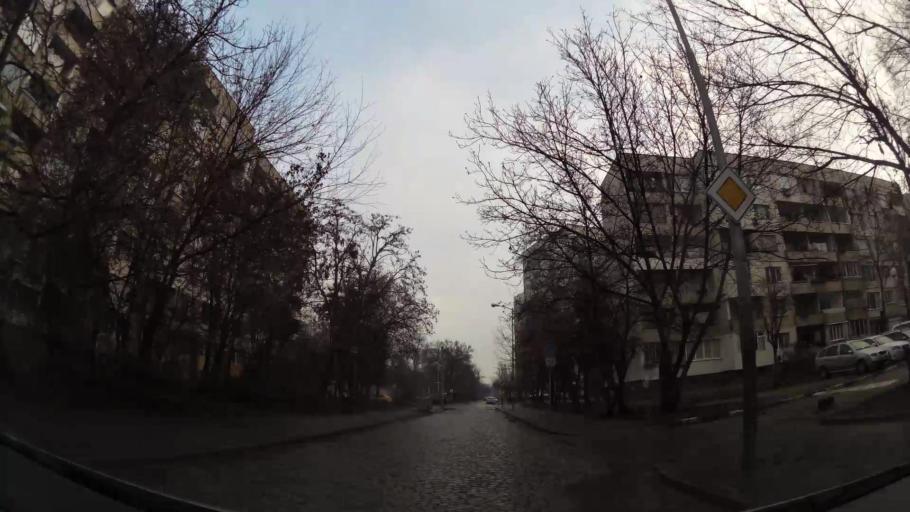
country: BG
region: Sofia-Capital
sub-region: Stolichna Obshtina
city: Sofia
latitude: 42.7275
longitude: 23.3080
